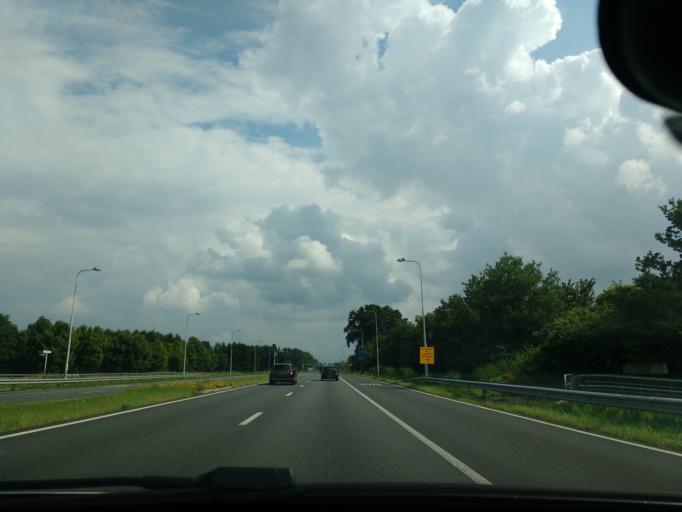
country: NL
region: Gelderland
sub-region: Gemeente Ede
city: Bennekom
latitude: 52.0064
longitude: 5.6541
